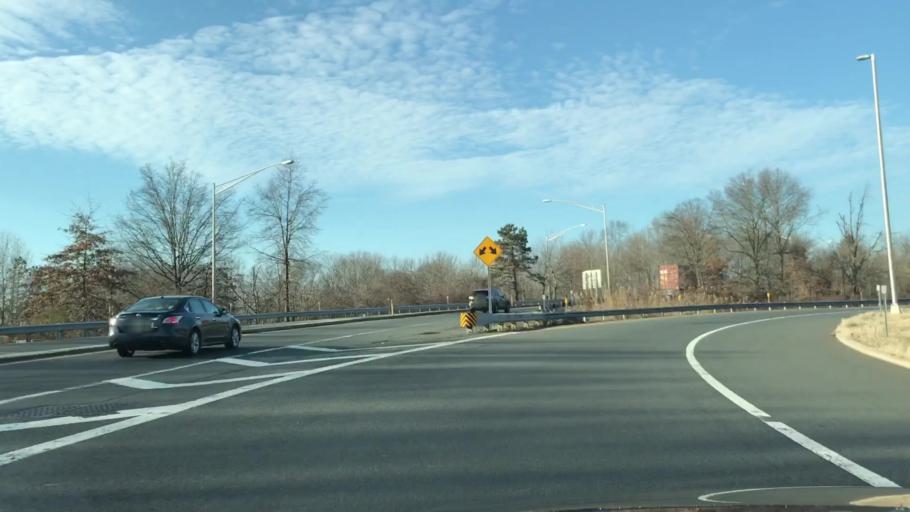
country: US
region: New Jersey
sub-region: Mercer County
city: Robbinsville
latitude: 40.1953
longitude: -74.6104
